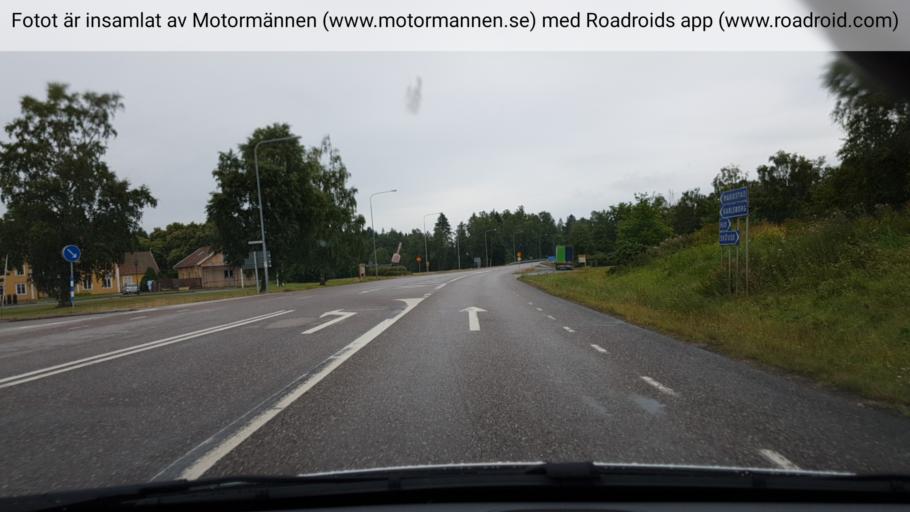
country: SE
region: Vaestra Goetaland
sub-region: Tibro Kommun
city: Tibro
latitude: 58.4290
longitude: 14.1455
